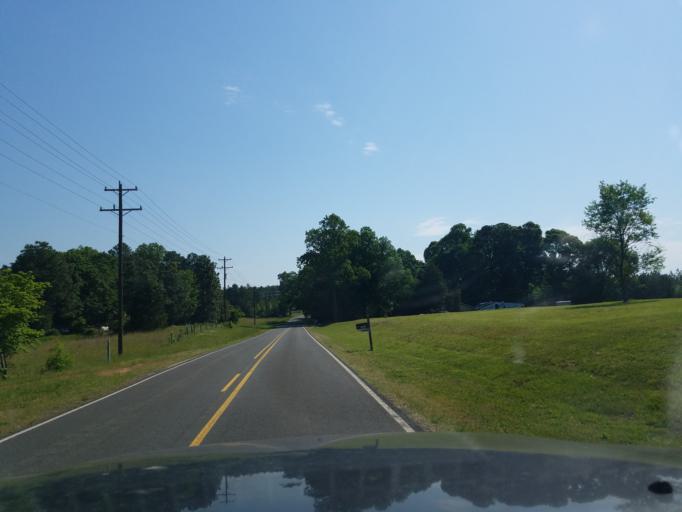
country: US
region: North Carolina
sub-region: Vance County
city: Henderson
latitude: 36.3973
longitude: -78.4317
